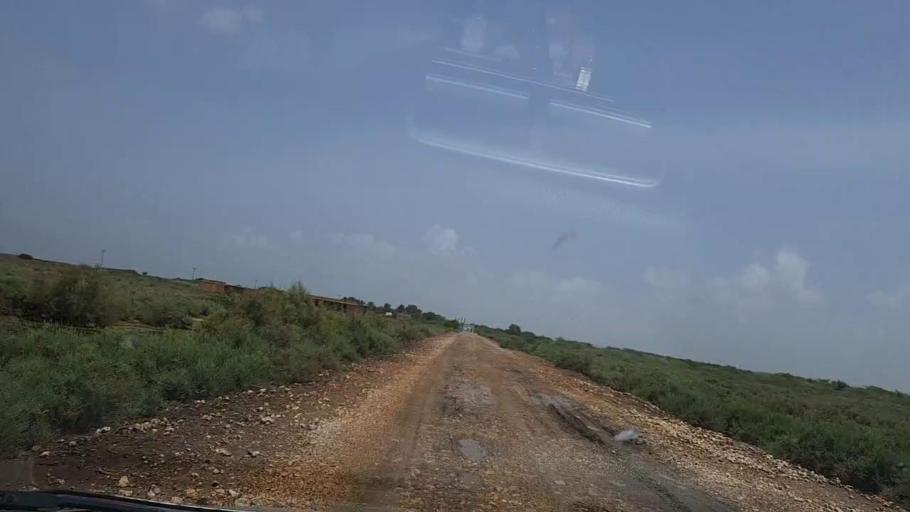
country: PK
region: Sindh
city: Keti Bandar
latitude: 24.1525
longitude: 67.5315
